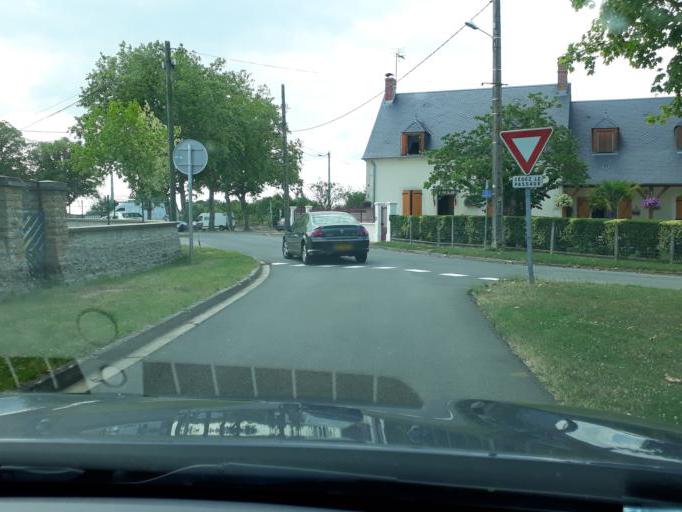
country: FR
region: Centre
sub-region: Departement du Cher
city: Nerondes
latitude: 47.0672
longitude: 2.8042
